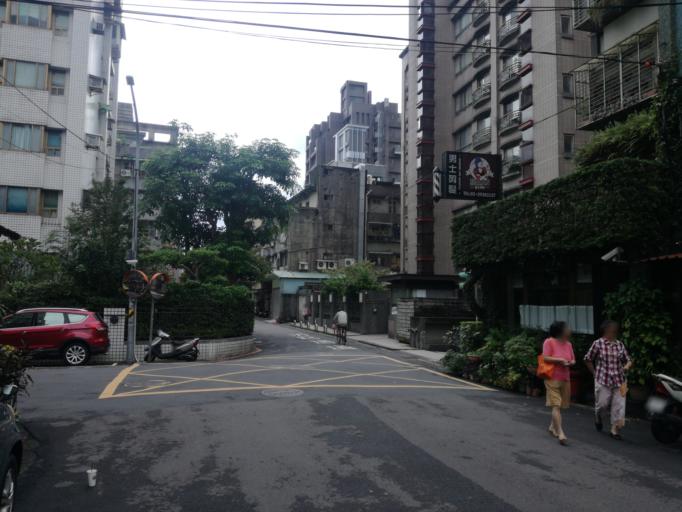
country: TW
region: Taipei
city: Taipei
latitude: 24.9830
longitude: 121.5620
